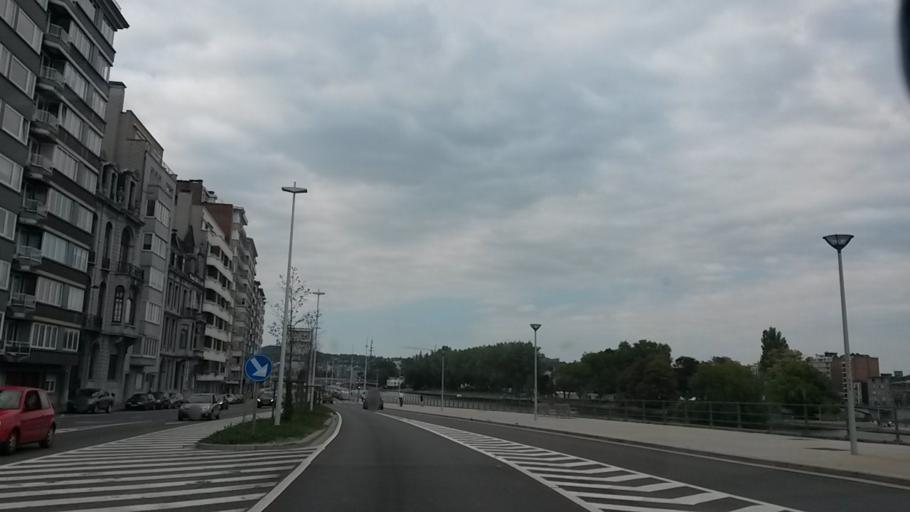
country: BE
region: Wallonia
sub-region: Province de Liege
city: Liege
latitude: 50.6216
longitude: 5.5774
